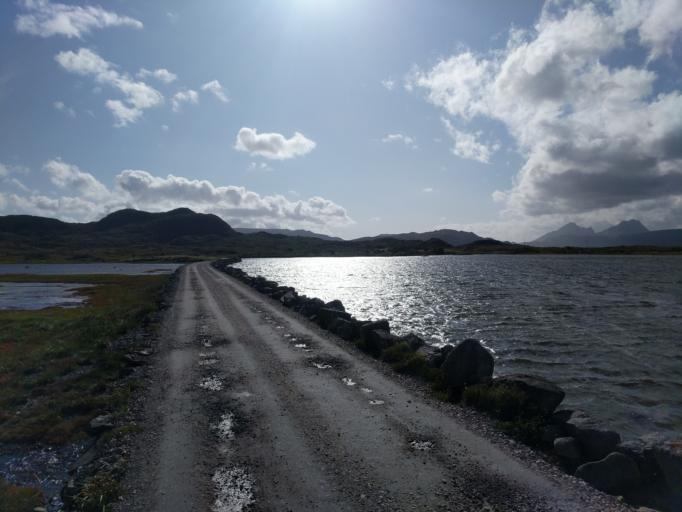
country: NO
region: Nordland
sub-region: Vestvagoy
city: Evjen
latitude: 68.3311
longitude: 13.8919
